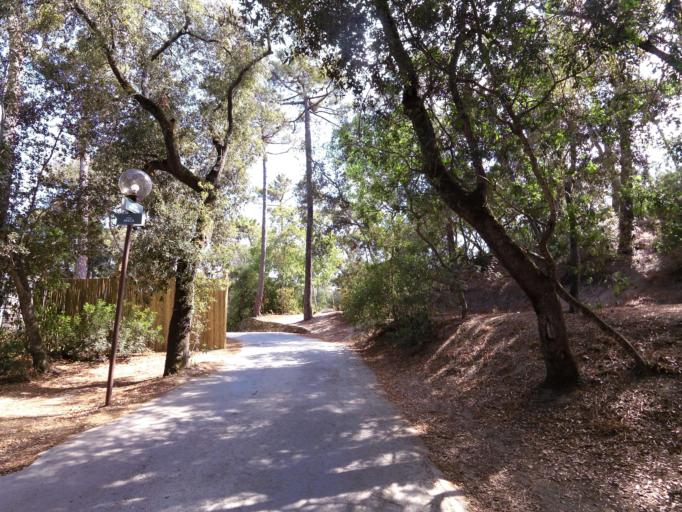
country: IT
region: Tuscany
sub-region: Provincia di Livorno
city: Donoratico
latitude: 43.1529
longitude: 10.5423
